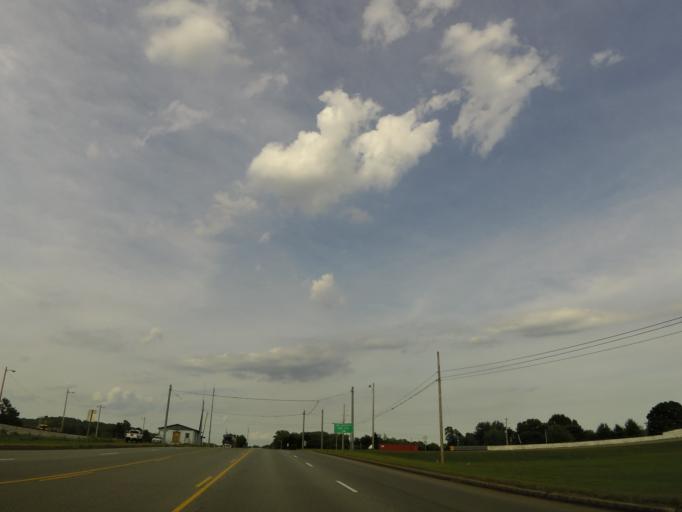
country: US
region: Tennessee
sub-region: Humphreys County
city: New Johnsonville
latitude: 36.0188
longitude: -87.9830
